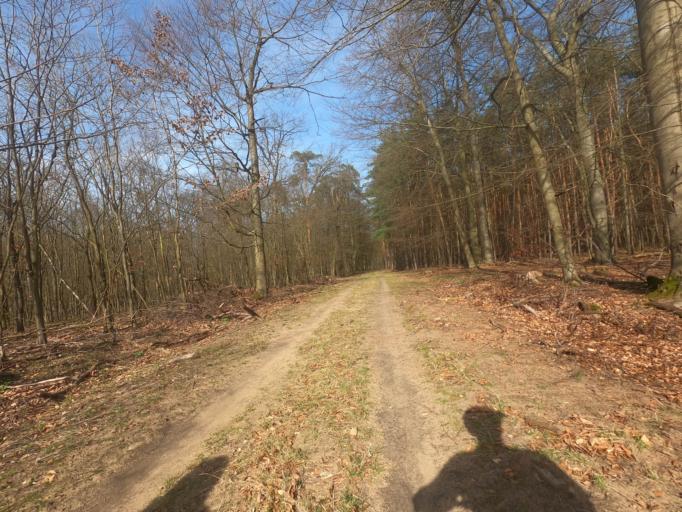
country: DE
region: Hesse
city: Raunheim
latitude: 49.9979
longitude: 8.5031
